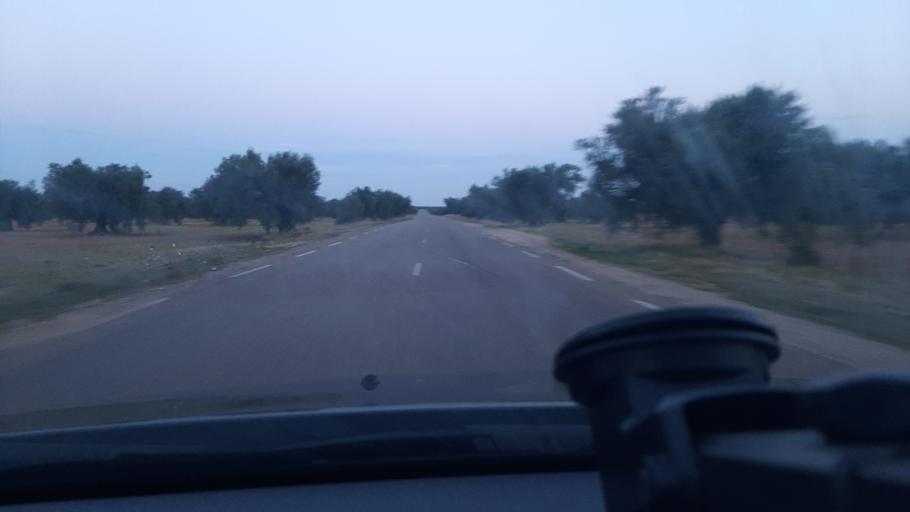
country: TN
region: Al Mahdiyah
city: Shurban
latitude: 35.0326
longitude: 10.5057
